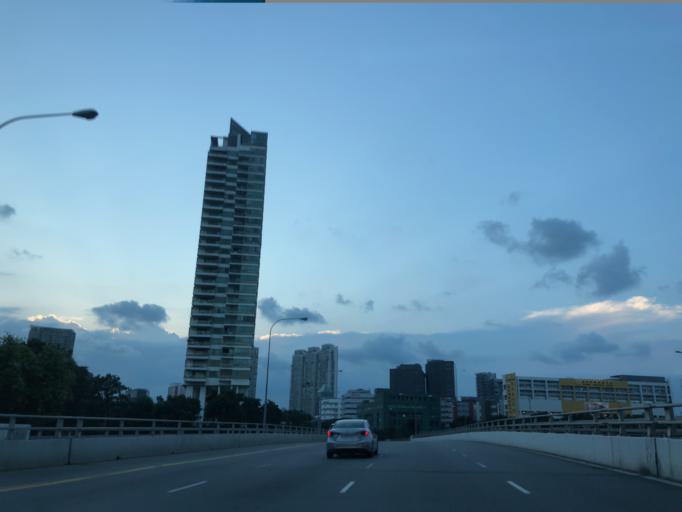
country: SG
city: Singapore
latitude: 1.3100
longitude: 103.8710
